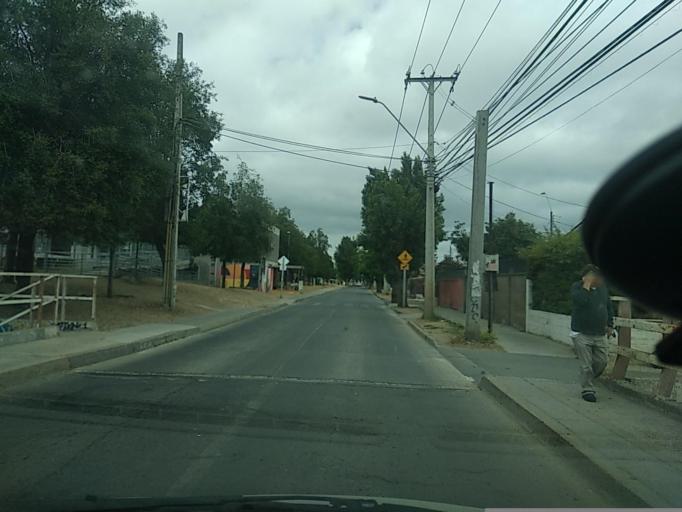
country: CL
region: Valparaiso
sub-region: Provincia de Marga Marga
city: Villa Alemana
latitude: -33.0418
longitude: -71.3654
